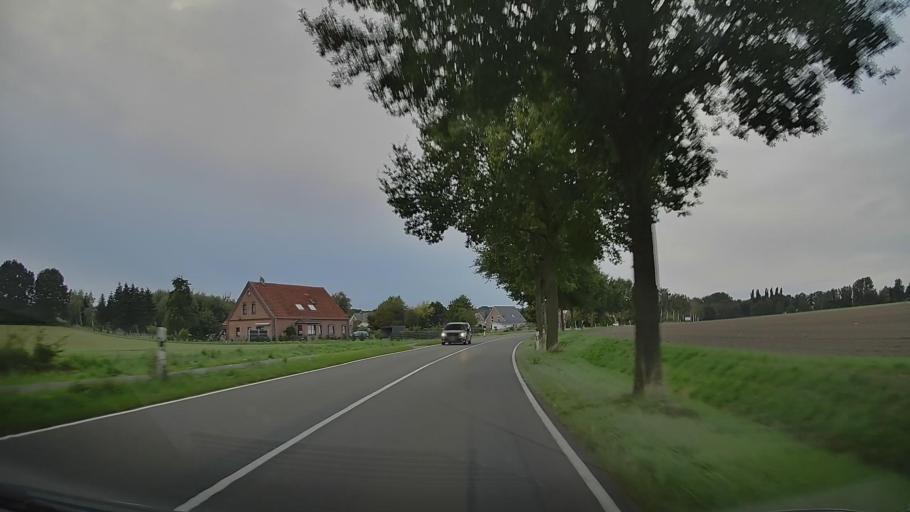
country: DE
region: Lower Saxony
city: Sustedt
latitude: 52.8988
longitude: 8.8975
